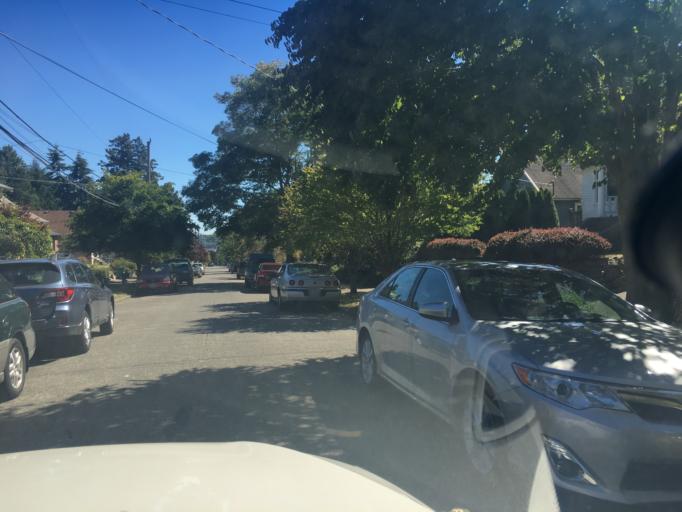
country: US
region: Washington
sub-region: King County
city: Shoreline
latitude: 47.6808
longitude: -122.3898
